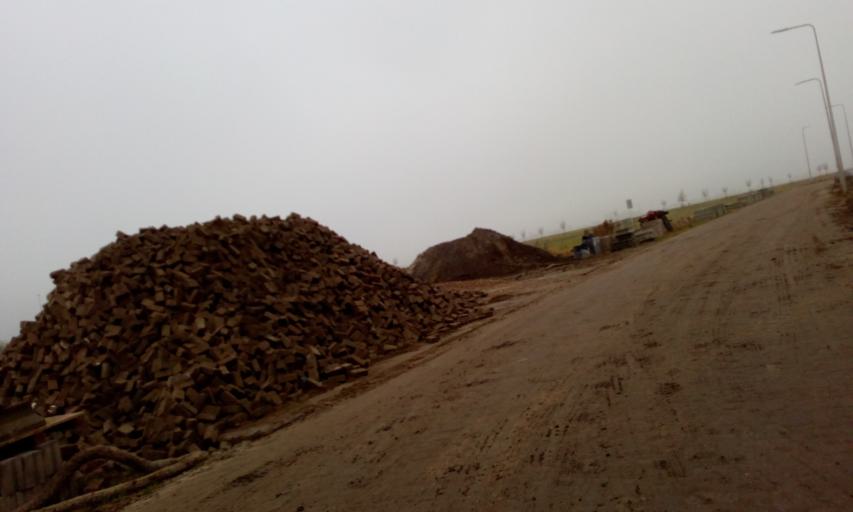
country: NL
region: South Holland
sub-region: Gemeente Lansingerland
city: Berkel en Rodenrijs
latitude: 51.9832
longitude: 4.4498
